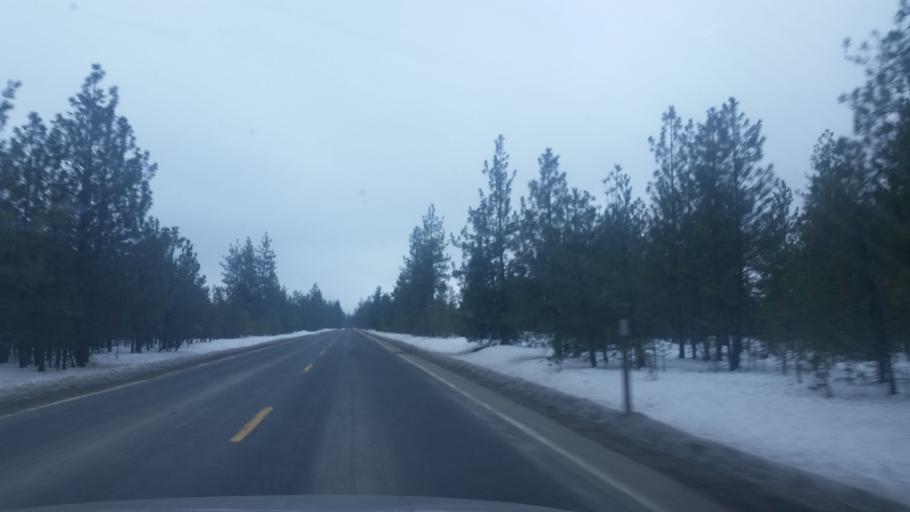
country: US
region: Washington
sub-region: Spokane County
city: Fairchild Air Force Base
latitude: 47.8622
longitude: -117.8441
